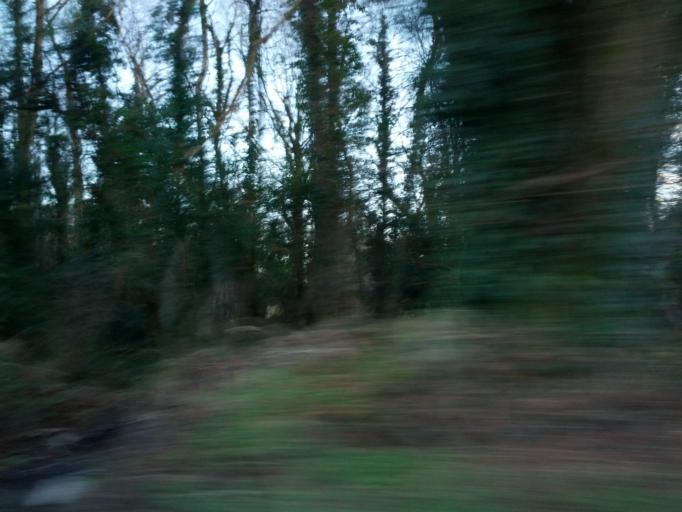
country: IE
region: Connaught
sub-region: County Galway
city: Athenry
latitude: 53.3235
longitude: -8.6994
